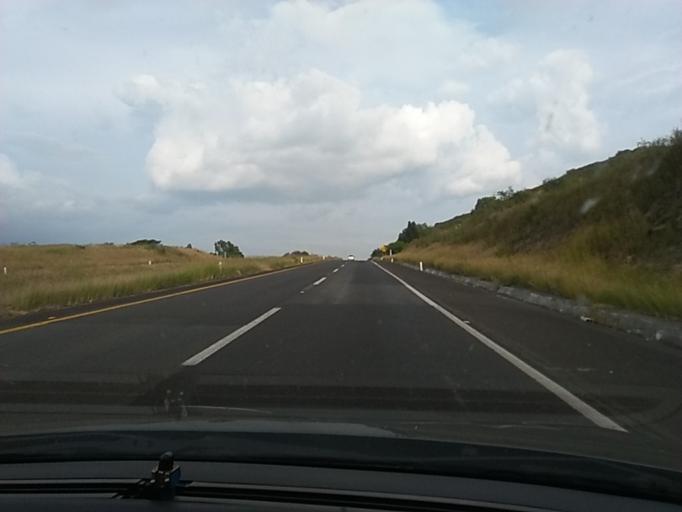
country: MX
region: Mexico
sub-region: Chapultepec
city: Chucandiro
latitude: 19.9038
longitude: -101.2825
